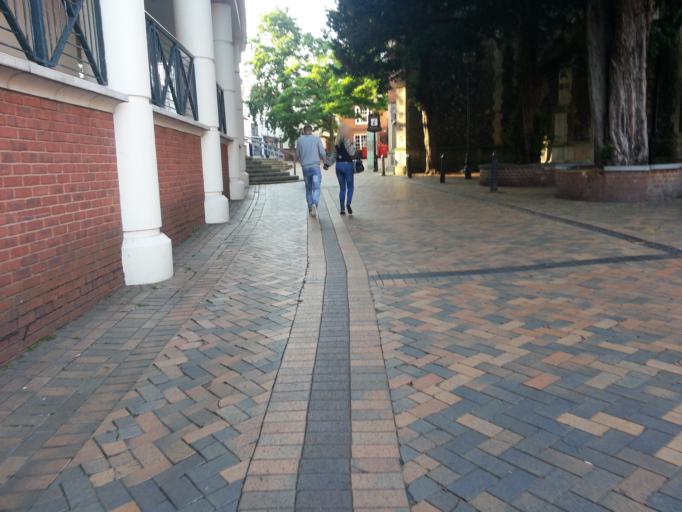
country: GB
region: England
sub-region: Suffolk
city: Ipswich
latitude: 52.0563
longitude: 1.1549
